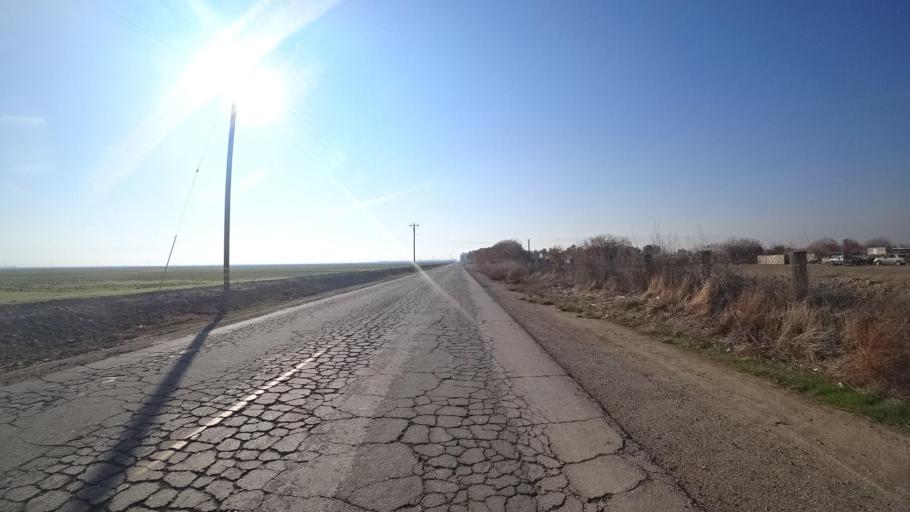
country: US
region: California
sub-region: Kern County
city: Weedpatch
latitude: 35.1626
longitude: -118.9677
